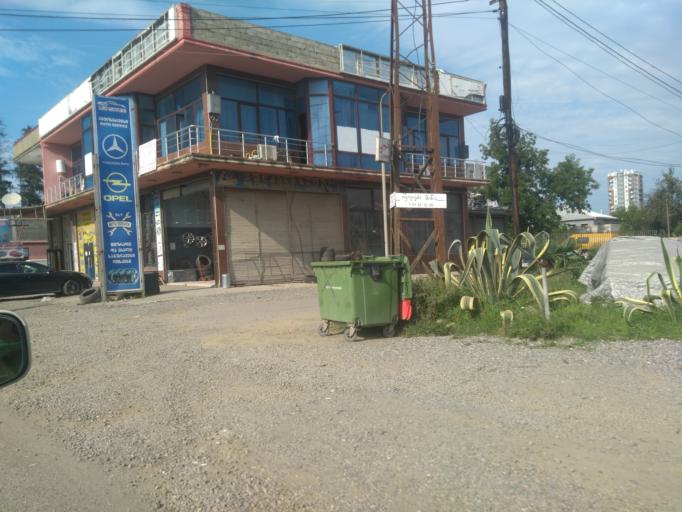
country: GE
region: Ajaria
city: Batumi
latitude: 41.6180
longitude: 41.6186
